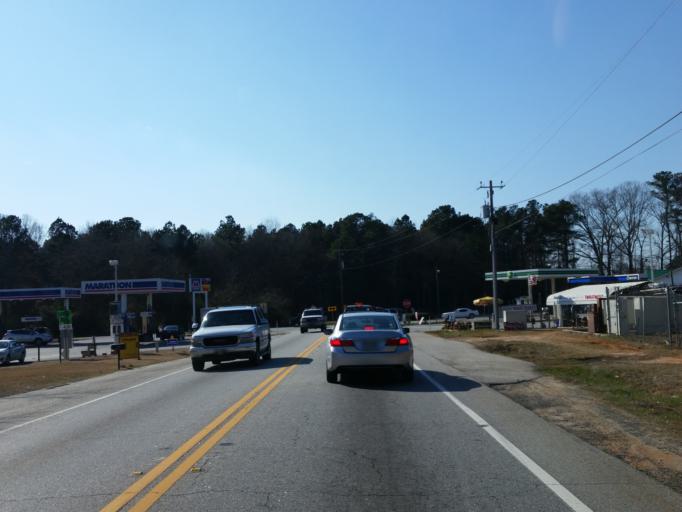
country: US
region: Georgia
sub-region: Clayton County
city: Lovejoy
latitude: 33.4249
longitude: -84.2839
